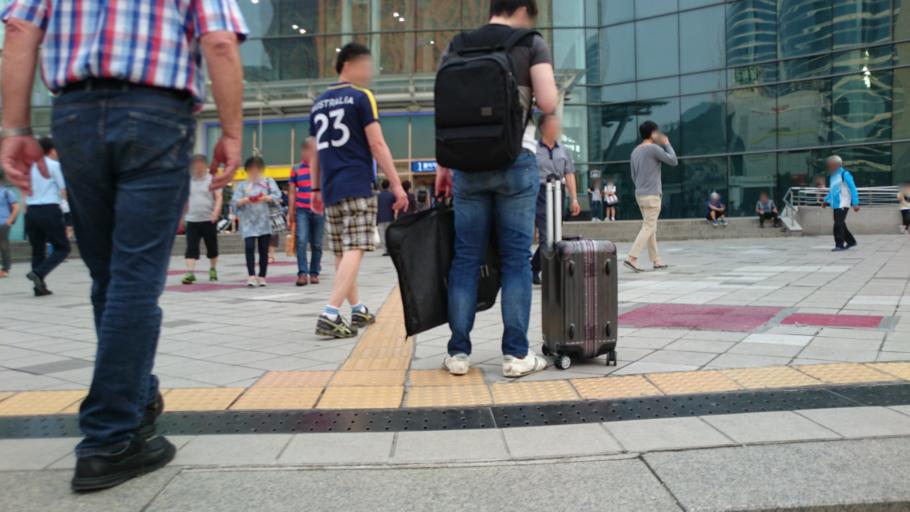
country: KR
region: Seoul
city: Seoul
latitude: 37.5546
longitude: 126.9720
